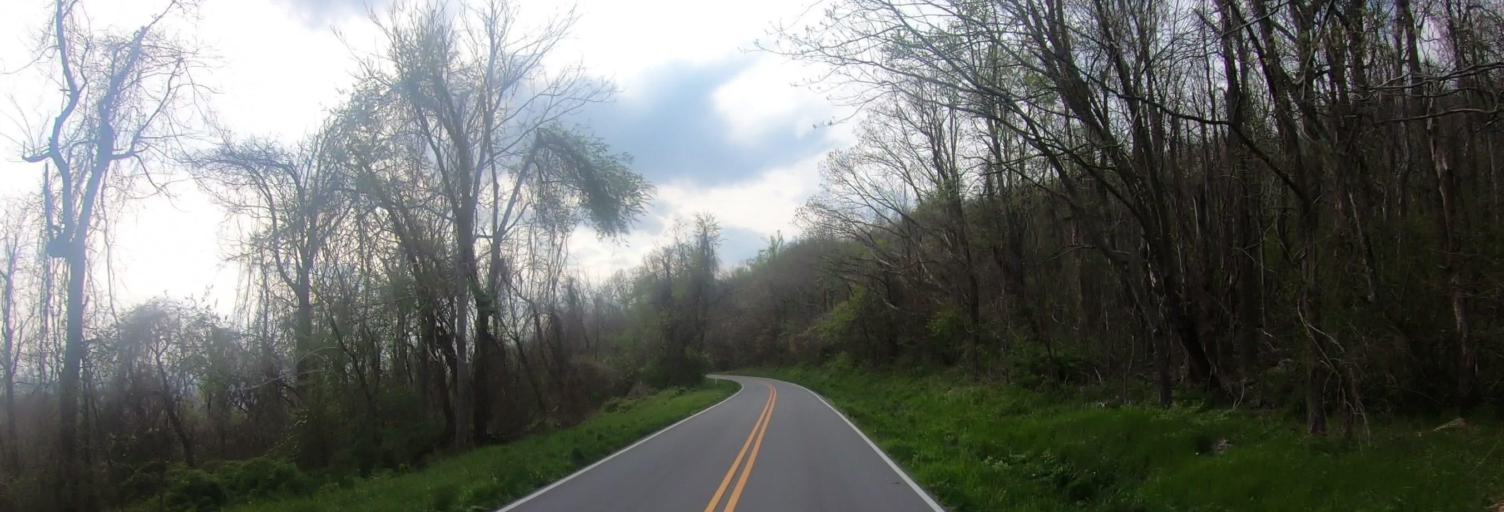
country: US
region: Virginia
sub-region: Augusta County
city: Dooms
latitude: 38.0741
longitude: -78.7951
